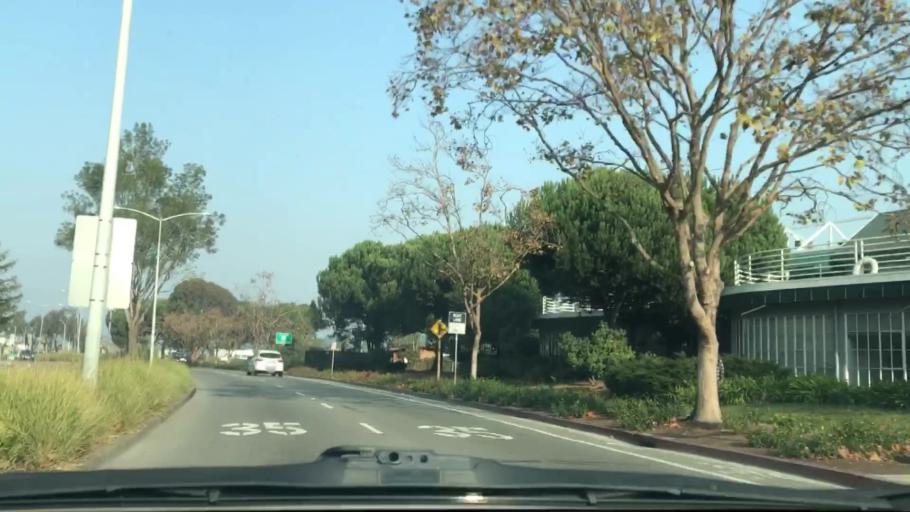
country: US
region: California
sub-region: Marin County
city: Marin City
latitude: 37.8711
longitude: -122.5039
